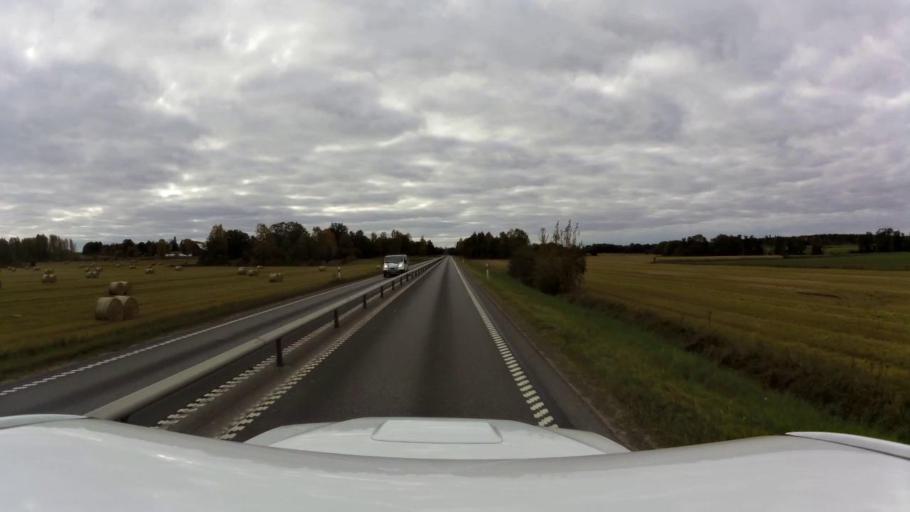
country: SE
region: OEstergoetland
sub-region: Linkopings Kommun
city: Malmslatt
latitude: 58.3678
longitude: 15.5442
